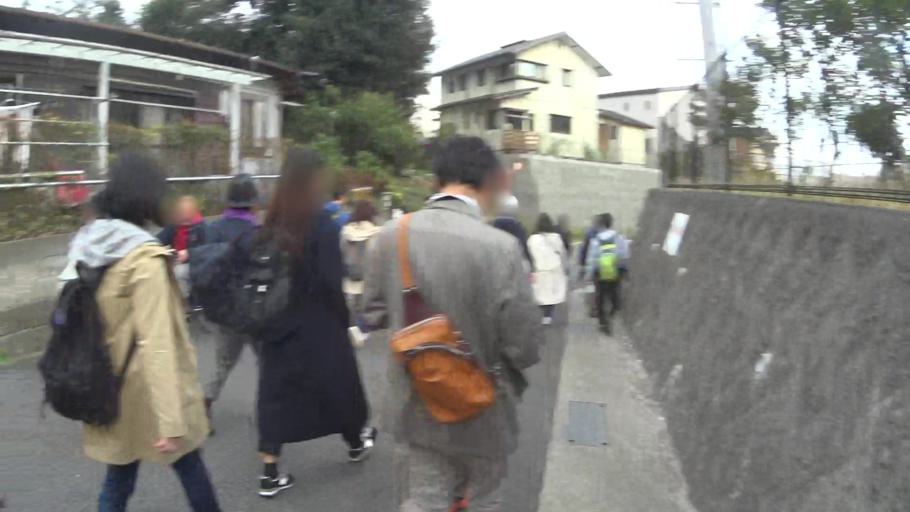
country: JP
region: Kanagawa
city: Fujisawa
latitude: 35.3134
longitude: 139.4915
